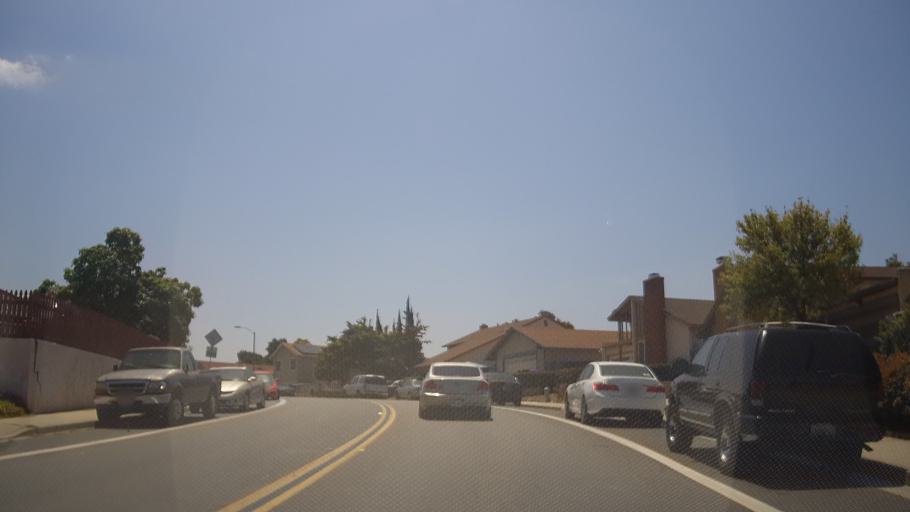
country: US
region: California
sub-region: San Diego County
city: Bonita
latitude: 32.6663
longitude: -117.0572
